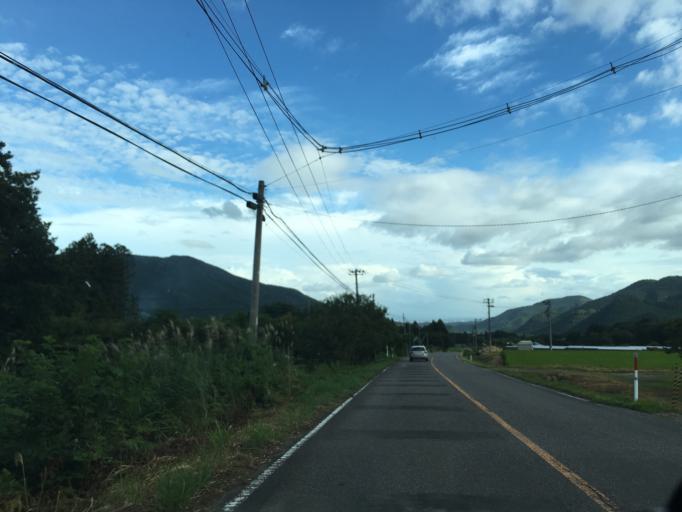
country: JP
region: Fukushima
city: Motomiya
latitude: 37.5420
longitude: 140.2612
